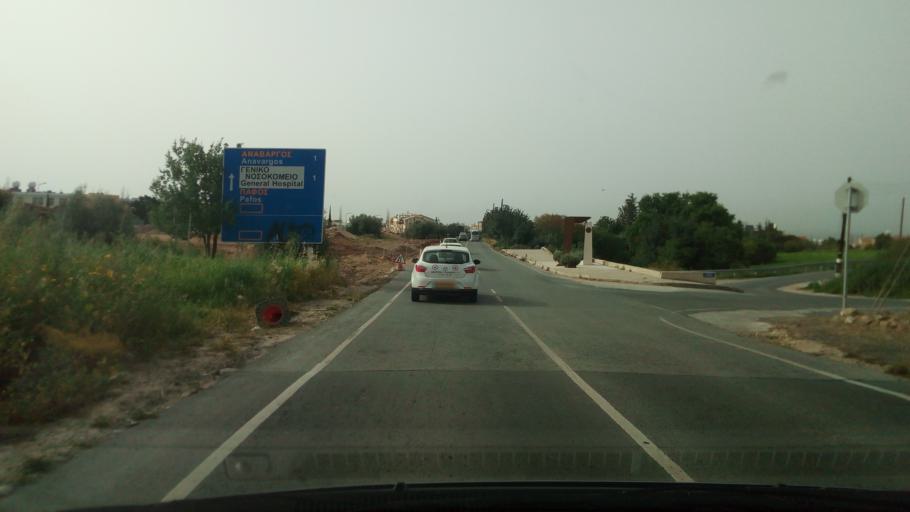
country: CY
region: Pafos
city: Mesogi
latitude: 34.8020
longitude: 32.4494
